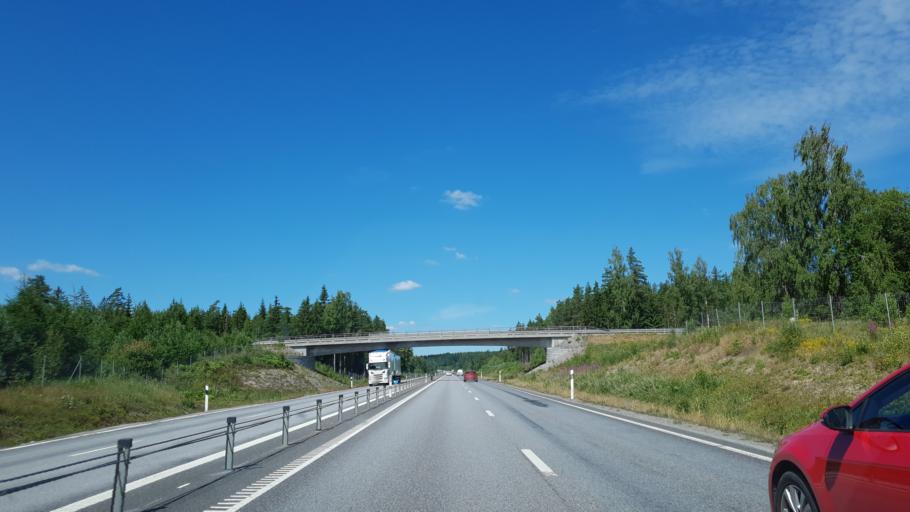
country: SE
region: Kronoberg
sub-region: Vaxjo Kommun
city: Gemla
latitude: 56.9128
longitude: 14.6311
